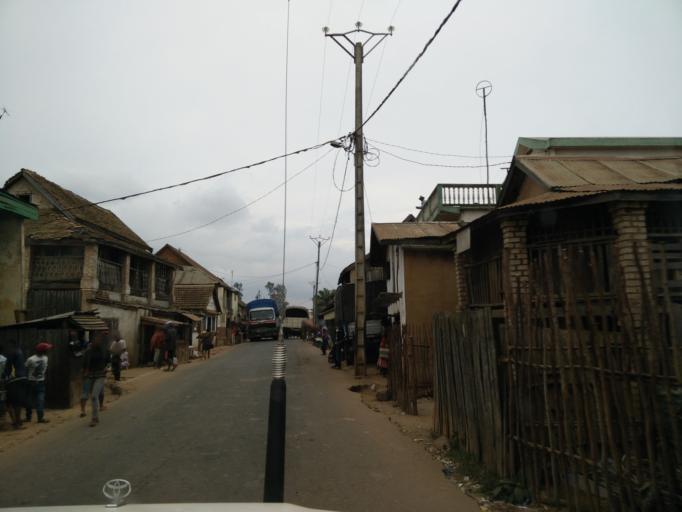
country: MG
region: Upper Matsiatra
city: Fianarantsoa
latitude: -21.5605
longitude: 47.0390
